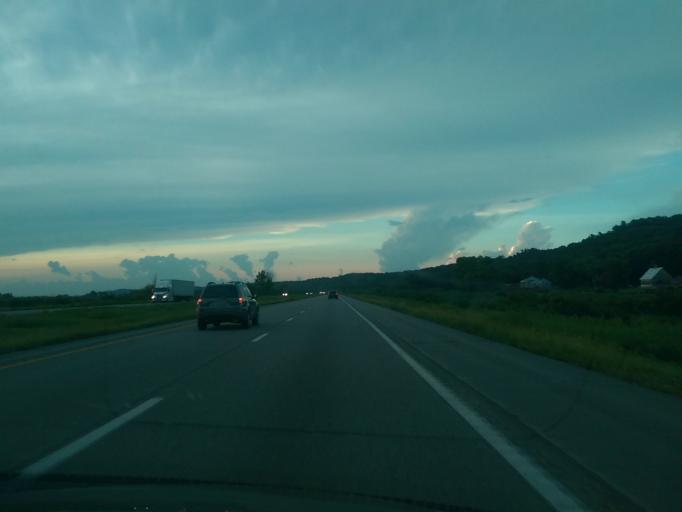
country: US
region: Missouri
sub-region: Atchison County
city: Rock Port
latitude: 40.3145
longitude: -95.4944
